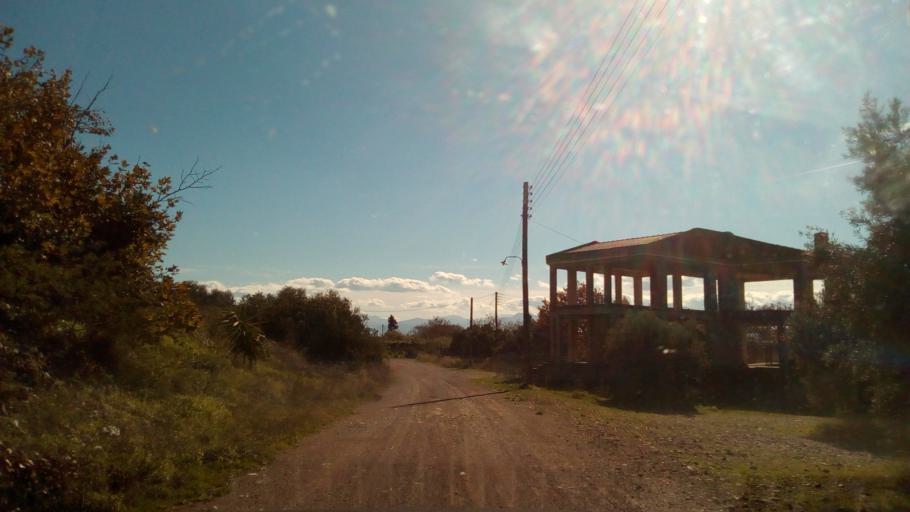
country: GR
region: West Greece
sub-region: Nomos Achaias
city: Kamarai
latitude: 38.3950
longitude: 22.0007
